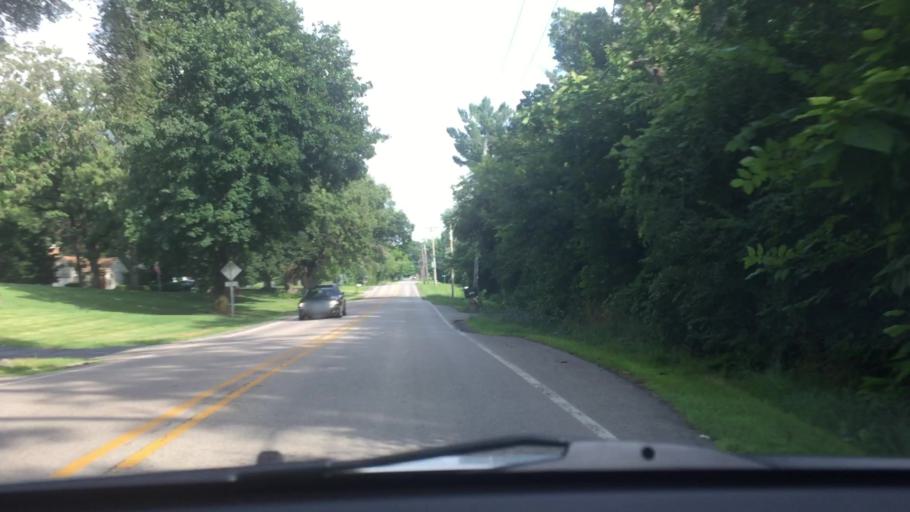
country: US
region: Illinois
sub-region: McHenry County
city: Crystal Lake
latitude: 42.2657
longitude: -88.3404
